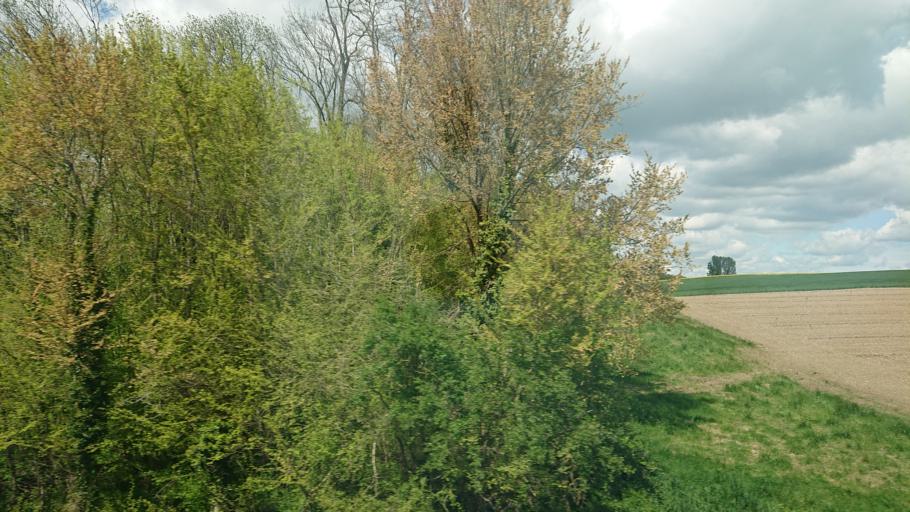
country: CH
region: Vaud
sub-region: Morges District
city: Saint-Prex
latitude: 46.4748
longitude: 6.4332
